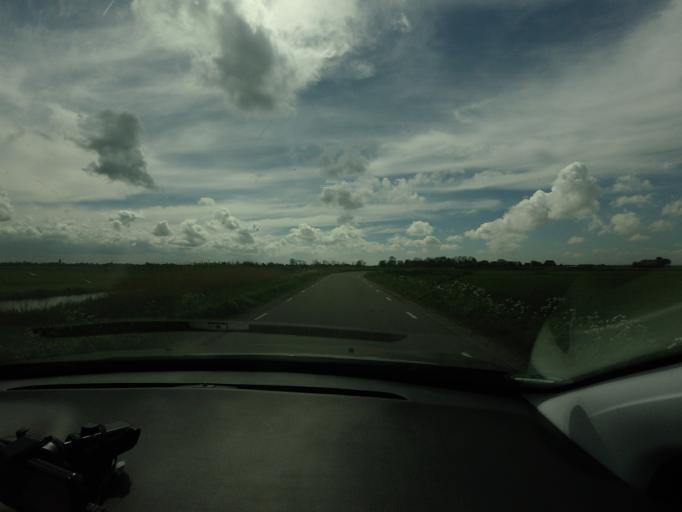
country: NL
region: North Holland
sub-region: Gemeente Heerhugowaard
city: Heerhugowaard
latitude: 52.5747
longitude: 4.8423
